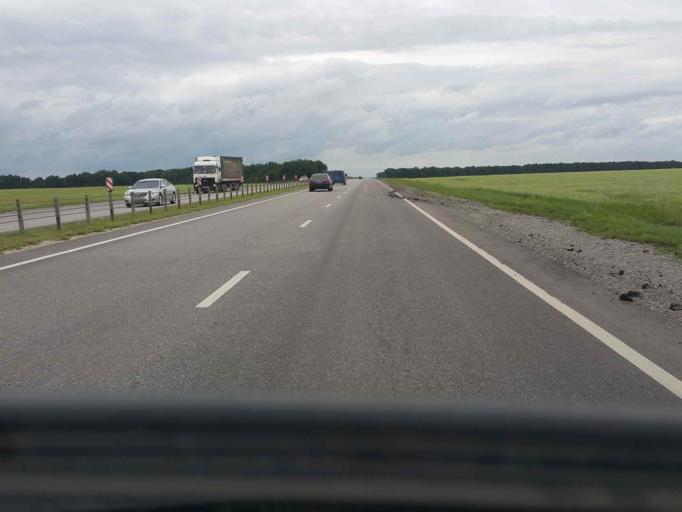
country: RU
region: Tambov
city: Zavoronezhskoye
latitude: 52.8994
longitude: 40.6652
